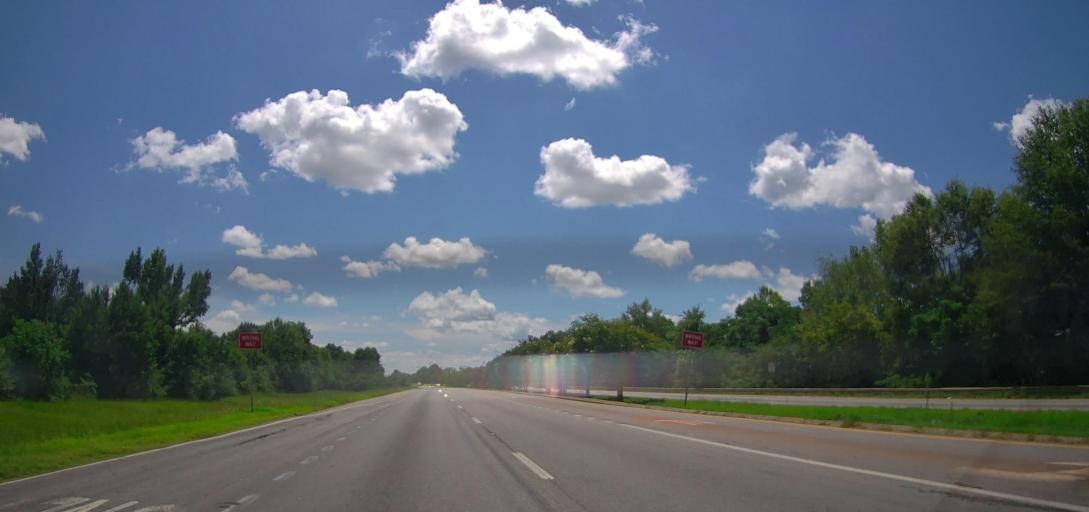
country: US
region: Alabama
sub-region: Montgomery County
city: Montgomery
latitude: 32.4105
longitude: -86.3035
